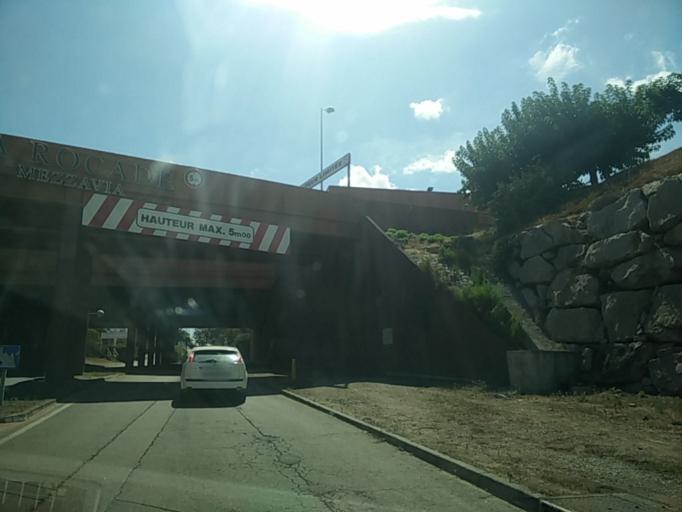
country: FR
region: Corsica
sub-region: Departement de la Corse-du-Sud
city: Afa
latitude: 41.9501
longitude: 8.7763
